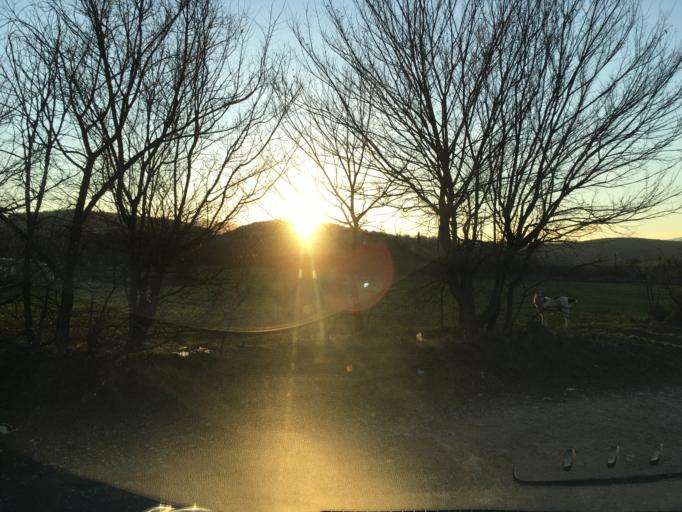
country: GR
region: West Macedonia
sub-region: Nomos Kozanis
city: Koila
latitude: 40.3300
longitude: 21.8096
